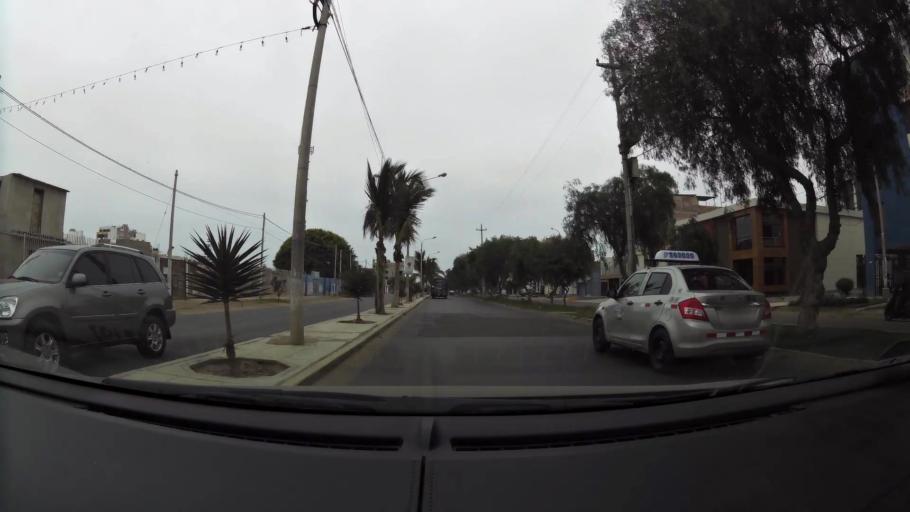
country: PE
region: La Libertad
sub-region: Provincia de Trujillo
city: Buenos Aires
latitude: -8.1314
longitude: -79.0448
